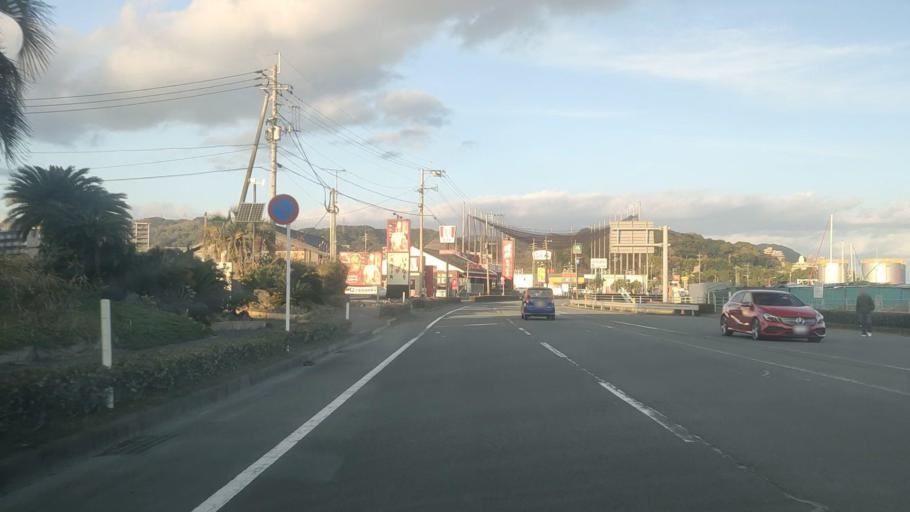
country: JP
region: Kagoshima
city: Kagoshima-shi
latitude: 31.6000
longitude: 130.5648
